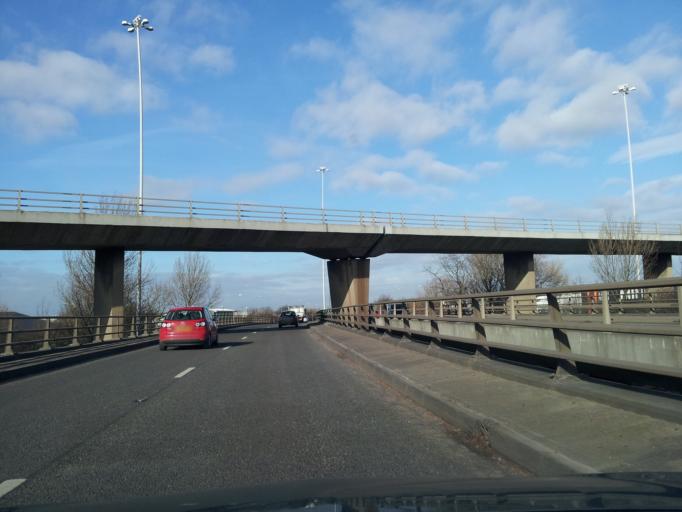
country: GB
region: England
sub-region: Nottingham
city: Nottingham
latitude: 52.9287
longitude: -1.1690
